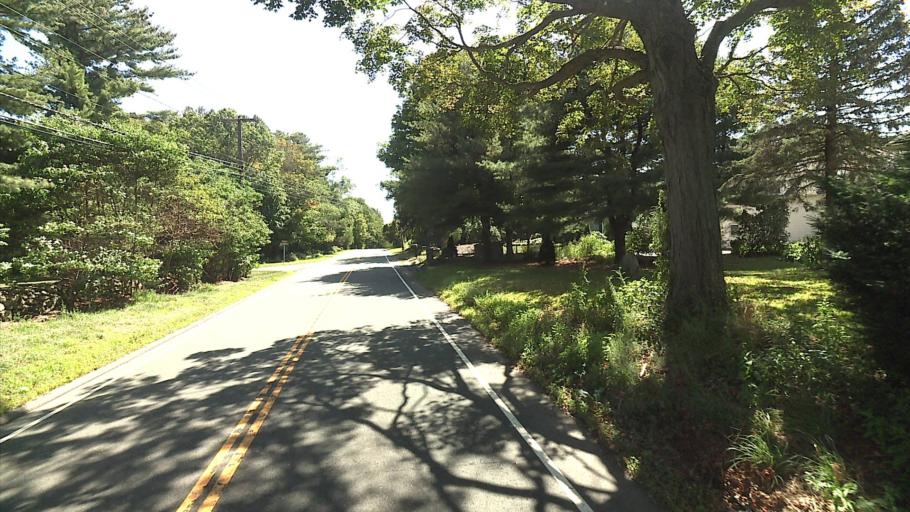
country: US
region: Connecticut
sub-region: New Haven County
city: Oxford
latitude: 41.4043
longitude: -73.1414
